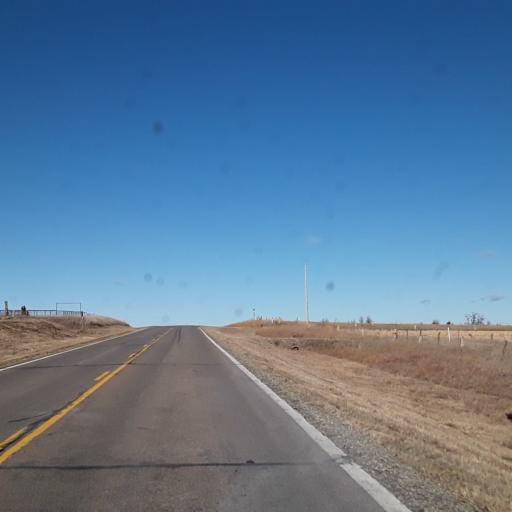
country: US
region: Kansas
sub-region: Lincoln County
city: Lincoln
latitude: 38.9416
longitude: -98.1512
